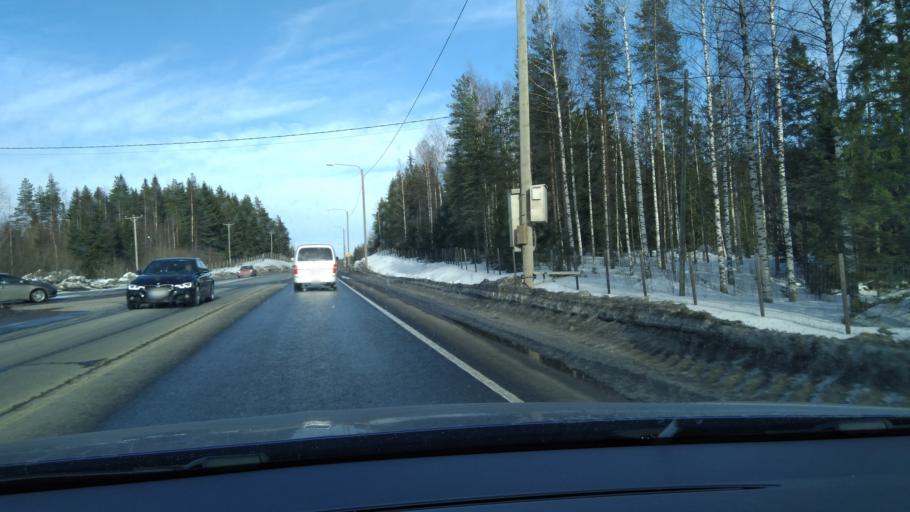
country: FI
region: Pirkanmaa
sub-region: Tampere
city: Orivesi
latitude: 61.6708
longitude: 24.2874
